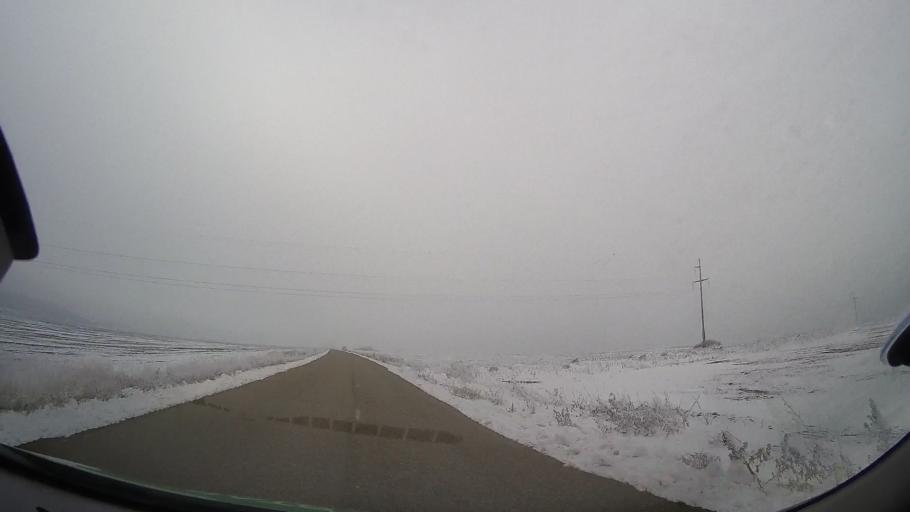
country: RO
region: Vaslui
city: Coroiesti
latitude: 46.2365
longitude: 27.4778
